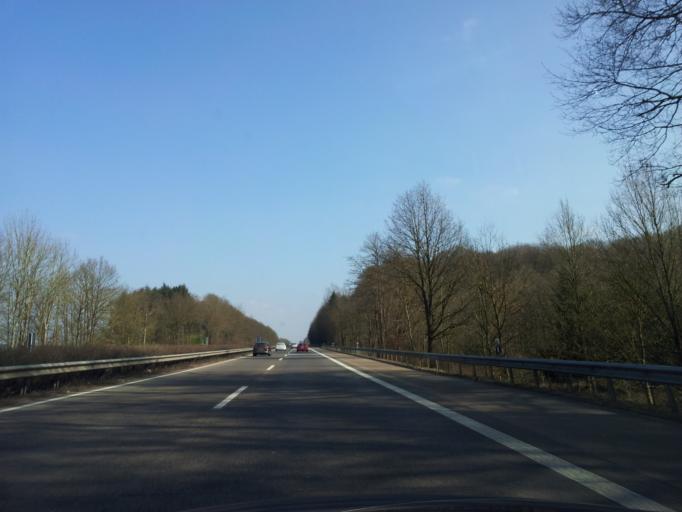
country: DE
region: Rheinland-Pfalz
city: Fohren
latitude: 49.8403
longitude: 6.7747
